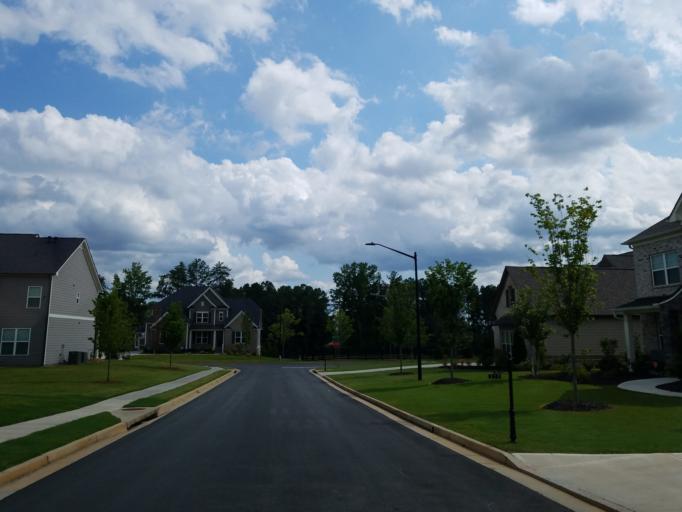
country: US
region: Georgia
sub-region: Cherokee County
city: Woodstock
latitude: 34.0761
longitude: -84.4880
